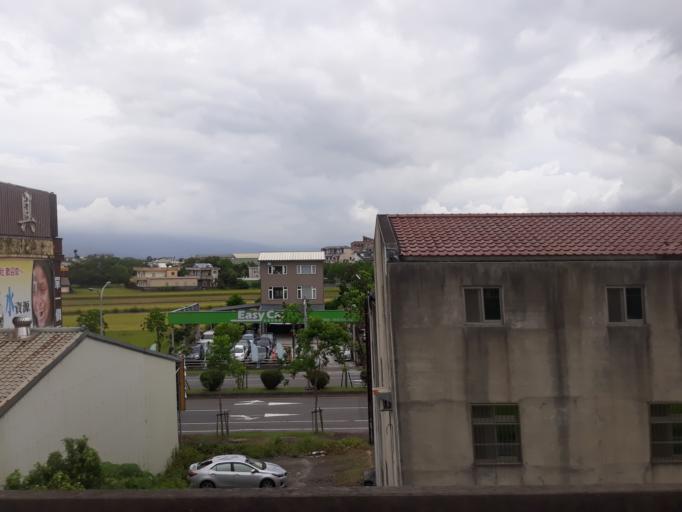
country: TW
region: Taiwan
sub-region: Yilan
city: Yilan
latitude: 24.7257
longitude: 121.7684
